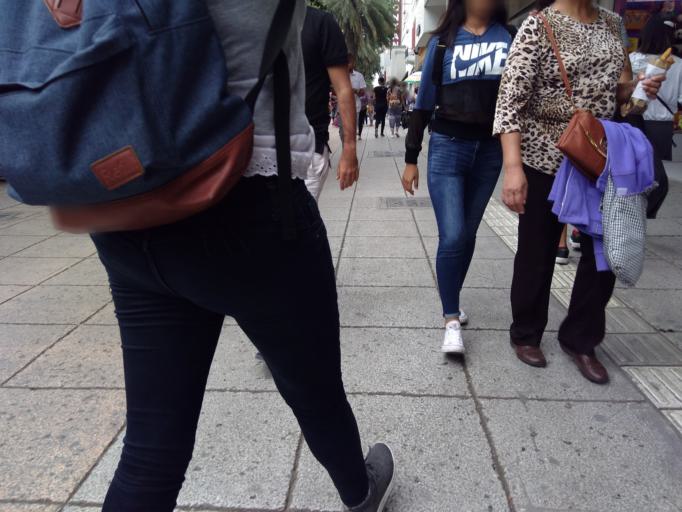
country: MX
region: Nuevo Leon
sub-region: Monterrey
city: Monterrey
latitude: 25.6675
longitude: -100.3135
